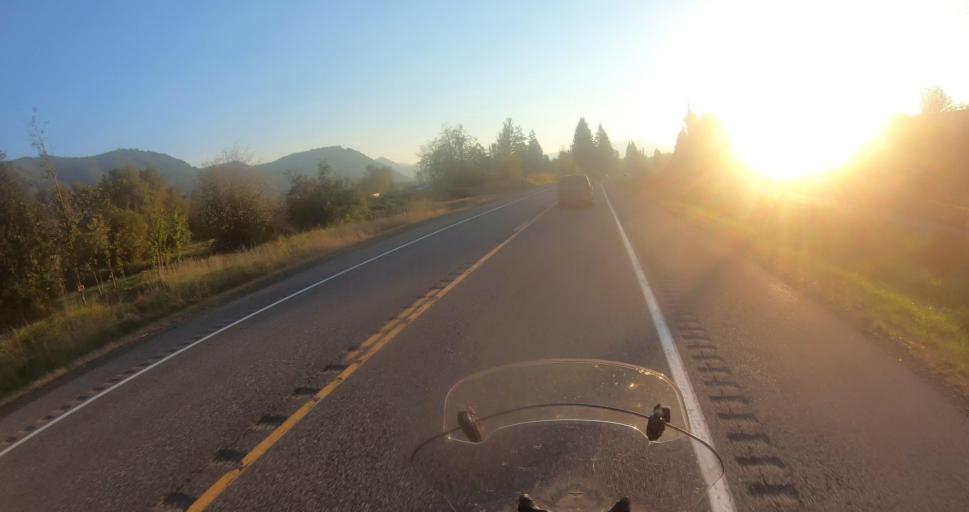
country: US
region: Washington
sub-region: Lewis County
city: Morton
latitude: 46.5208
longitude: -122.1529
